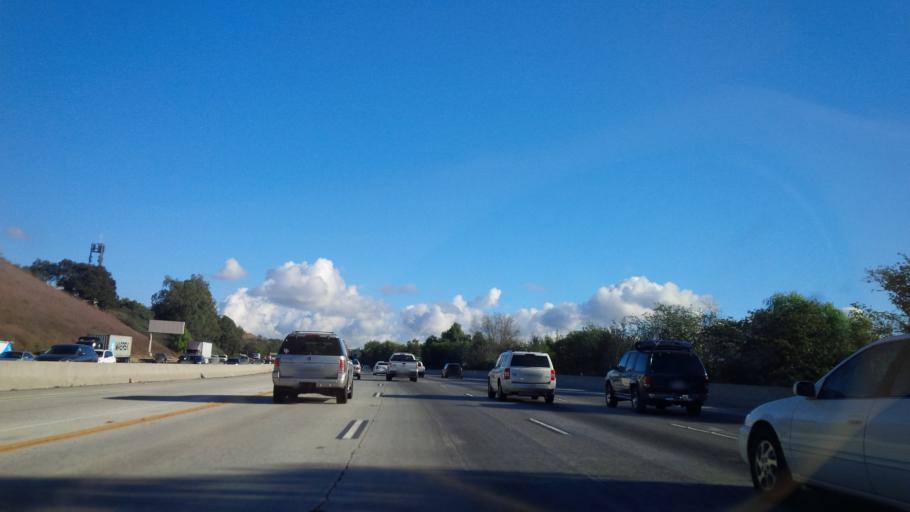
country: US
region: California
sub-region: Los Angeles County
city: Rowland Heights
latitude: 33.9623
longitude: -117.8531
